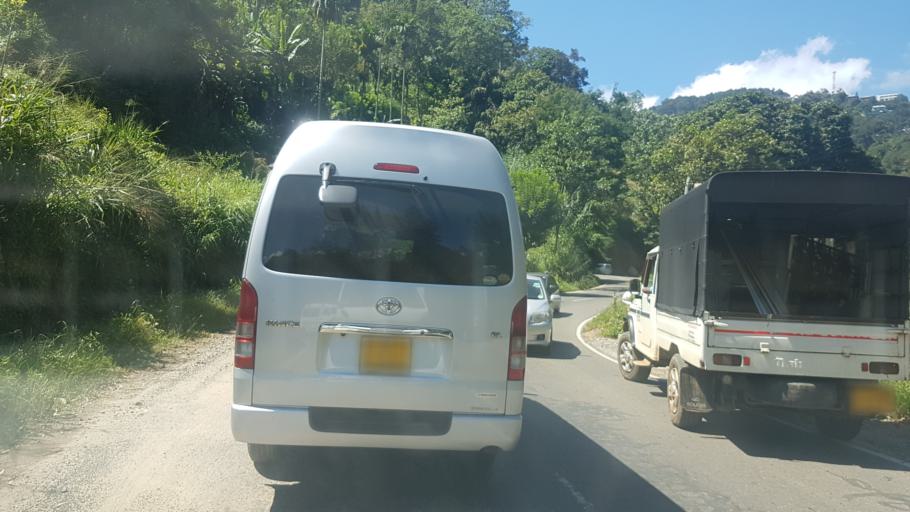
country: LK
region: Uva
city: Badulla
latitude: 6.8671
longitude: 81.0503
